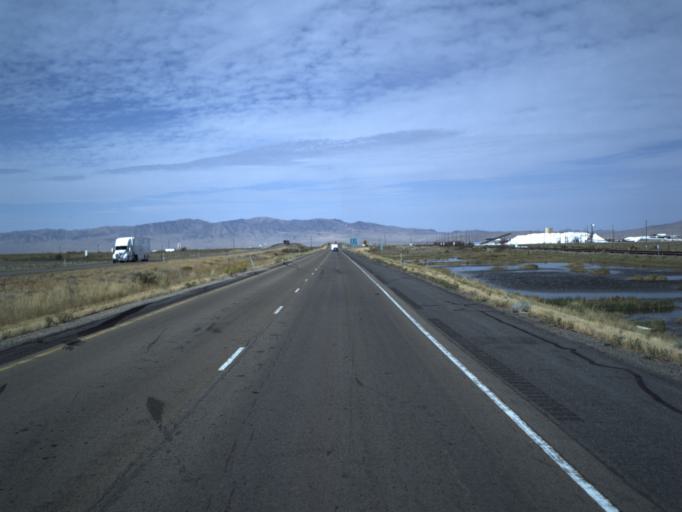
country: US
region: Utah
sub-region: Tooele County
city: Grantsville
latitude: 40.7448
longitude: -112.6399
